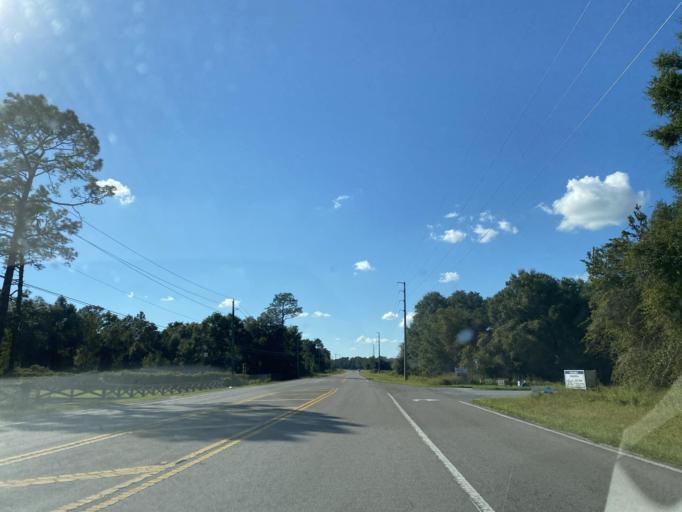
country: US
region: Florida
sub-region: Citrus County
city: Hernando
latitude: 29.0526
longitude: -82.2733
